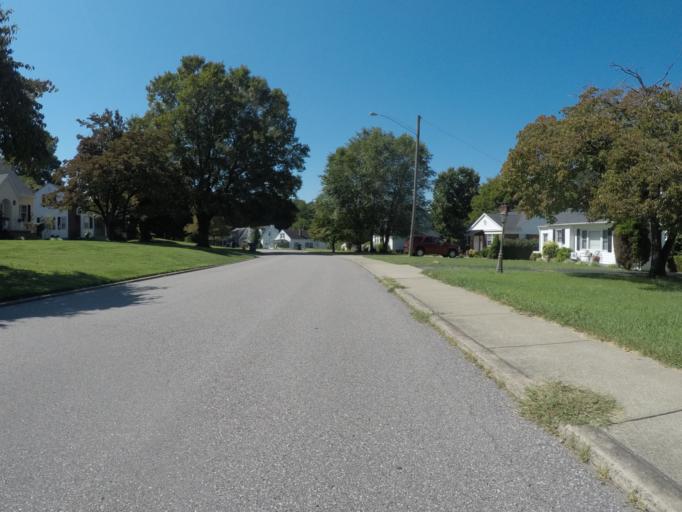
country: US
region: Kentucky
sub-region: Boyd County
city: Ashland
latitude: 38.4506
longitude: -82.6416
